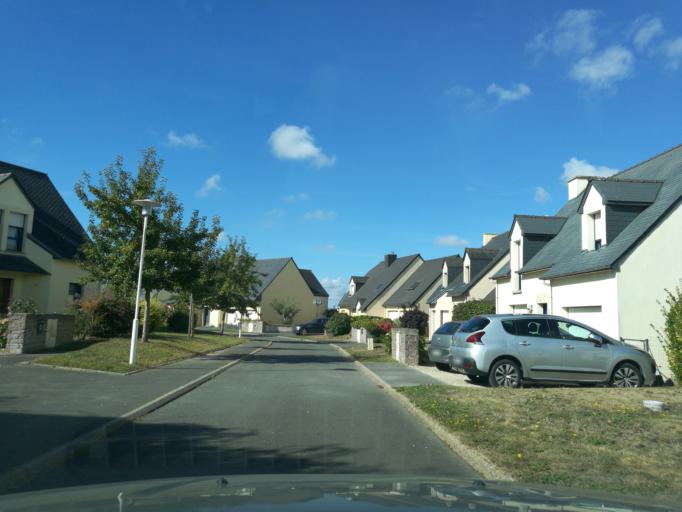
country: FR
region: Brittany
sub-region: Departement d'Ille-et-Vilaine
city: Pleumeleuc
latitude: 48.1875
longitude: -1.9251
